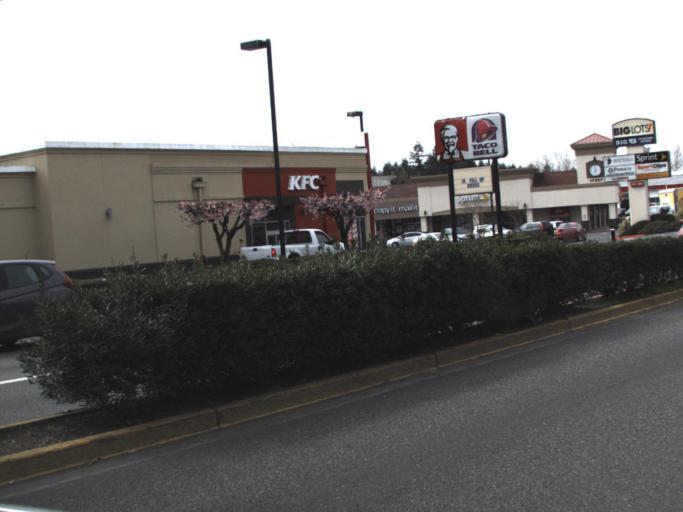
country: US
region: Washington
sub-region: King County
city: Covington
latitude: 47.3582
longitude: -122.1091
